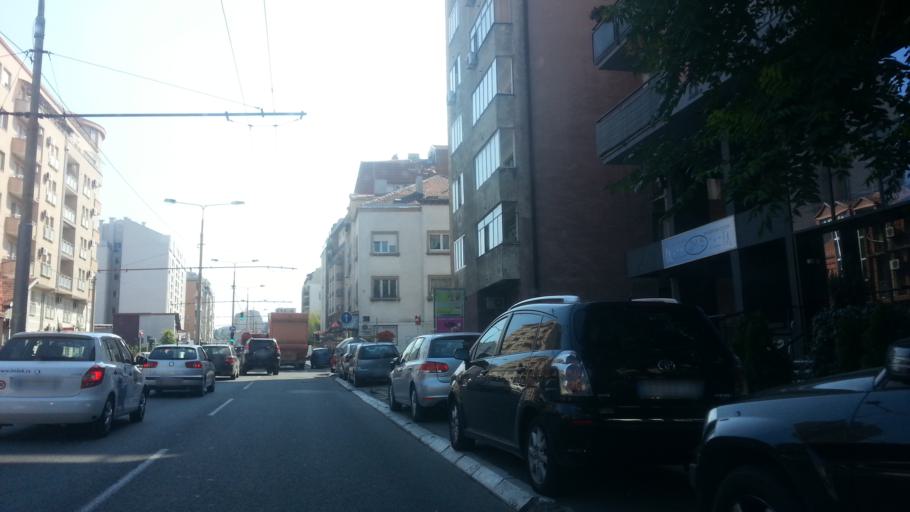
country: RS
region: Central Serbia
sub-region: Belgrade
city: Vracar
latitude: 44.8040
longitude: 20.4868
